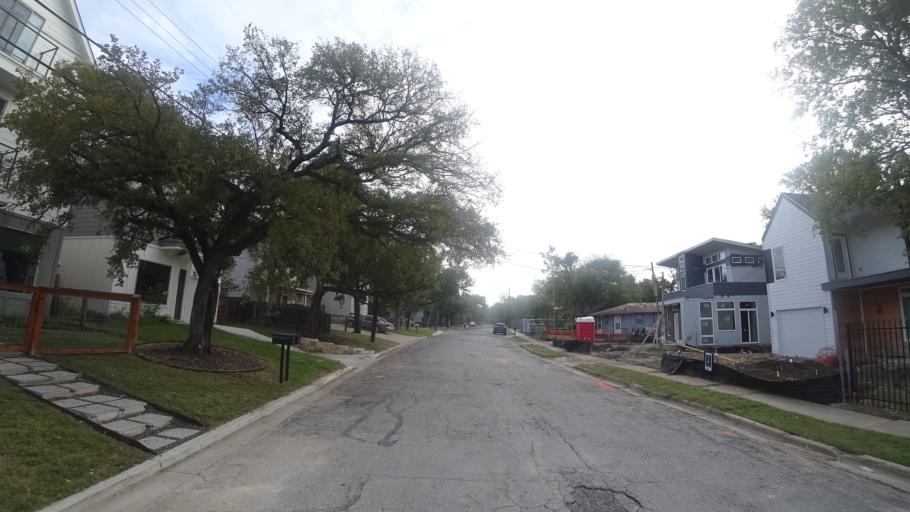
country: US
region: Texas
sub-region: Travis County
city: Austin
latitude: 30.2779
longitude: -97.7067
